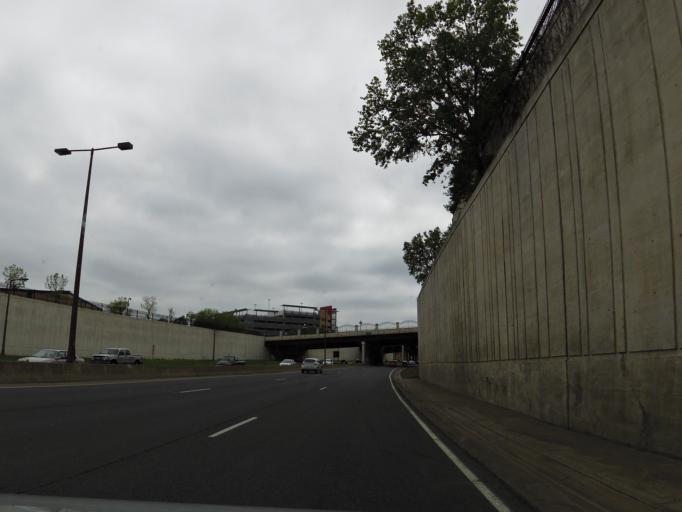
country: US
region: Minnesota
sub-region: Ramsey County
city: Saint Paul
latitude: 44.9487
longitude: -93.1027
